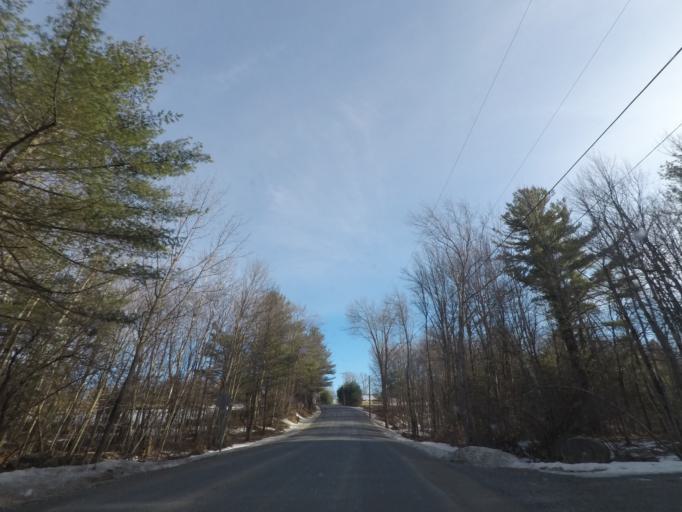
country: US
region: New York
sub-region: Rensselaer County
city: Poestenkill
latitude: 42.7610
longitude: -73.4241
